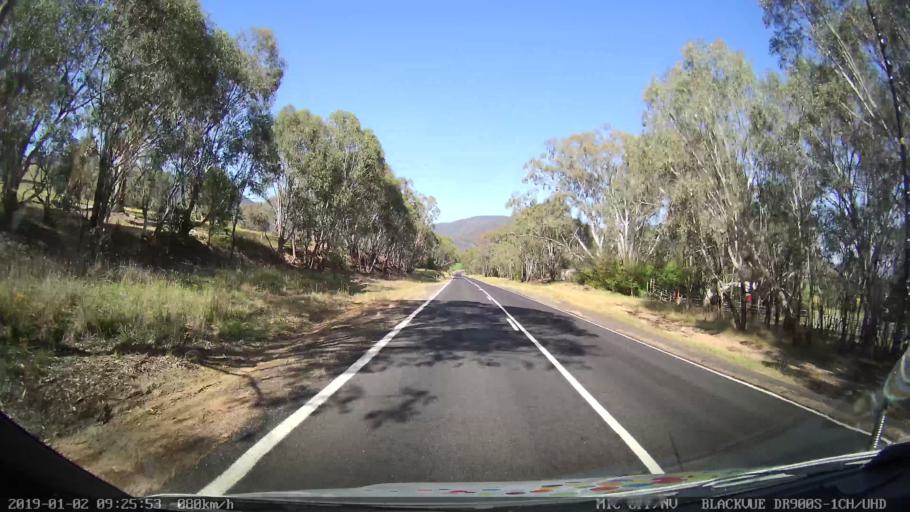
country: AU
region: New South Wales
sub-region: Tumut Shire
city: Tumut
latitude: -35.3642
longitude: 148.2803
